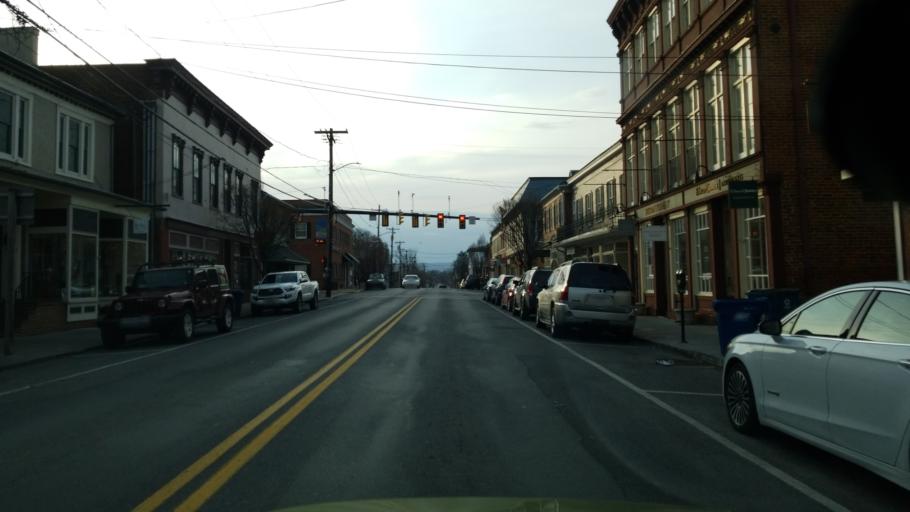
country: US
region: Virginia
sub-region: Clarke County
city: Berryville
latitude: 39.1514
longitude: -77.9820
